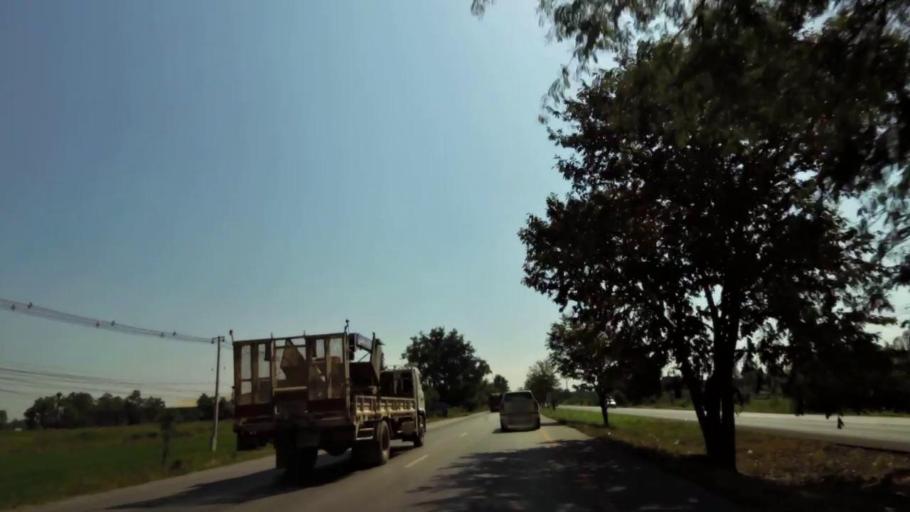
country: TH
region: Nakhon Sawan
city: Kao Liao
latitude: 15.8179
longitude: 100.1196
